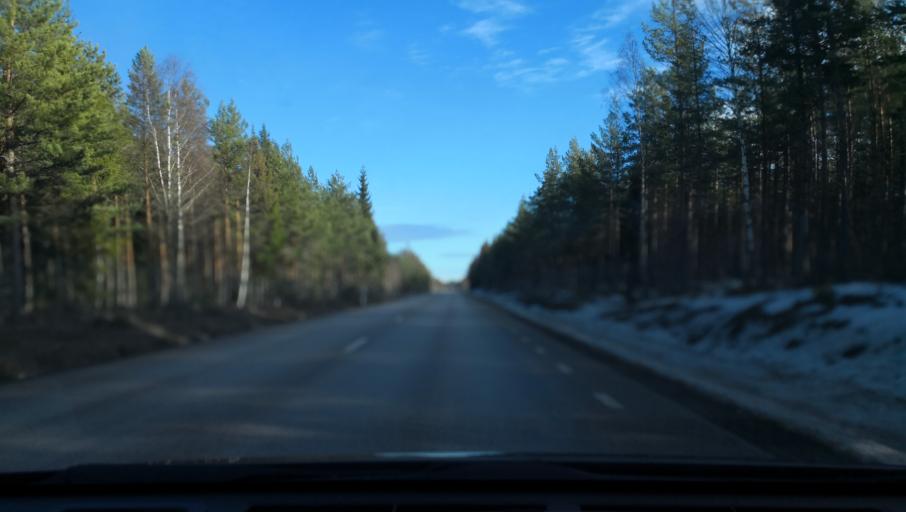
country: SE
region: Uppsala
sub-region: Osthammars Kommun
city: Osterbybruk
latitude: 60.1705
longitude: 17.9415
